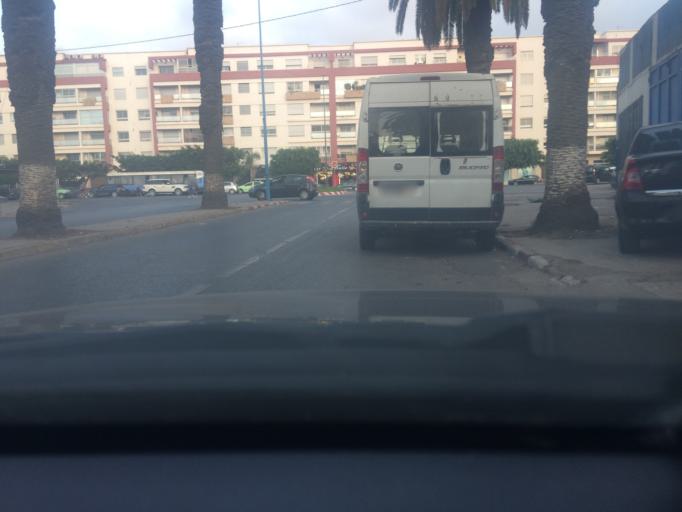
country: MA
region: Grand Casablanca
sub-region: Mohammedia
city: Mohammedia
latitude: 33.6923
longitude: -7.3944
